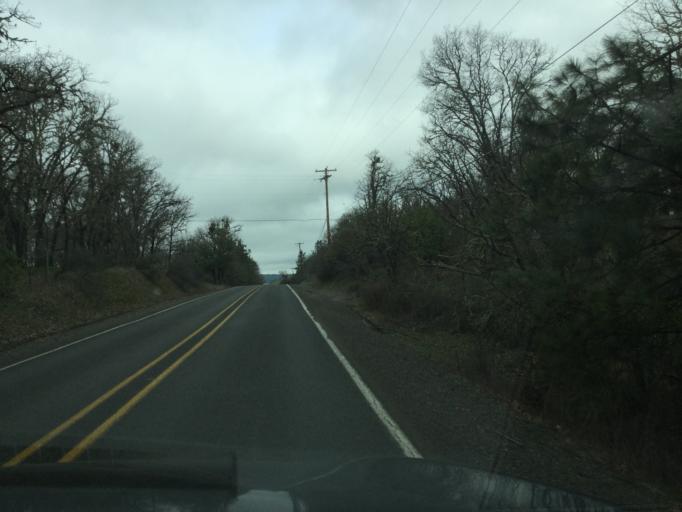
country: US
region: Oregon
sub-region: Jackson County
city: Central Point
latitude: 42.3905
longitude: -122.9884
